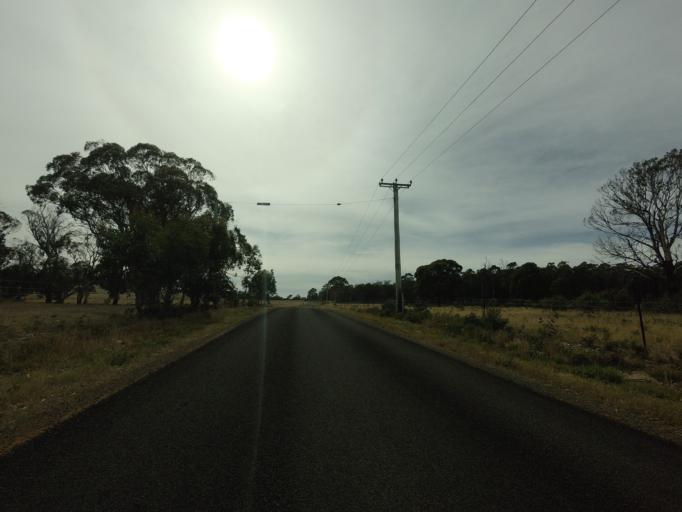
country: AU
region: Tasmania
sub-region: Sorell
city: Sorell
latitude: -42.4268
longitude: 147.4807
